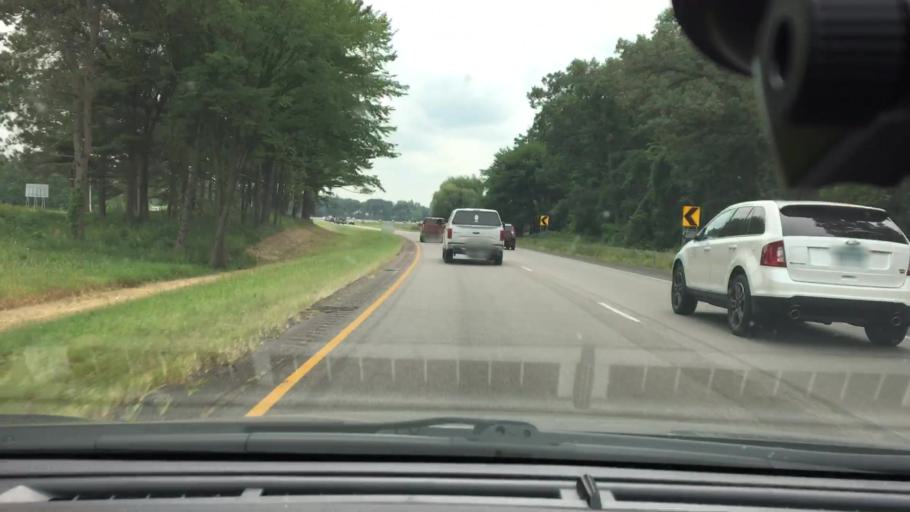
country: US
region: Minnesota
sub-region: Sherburne County
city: Zimmerman
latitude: 45.4931
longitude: -93.5828
